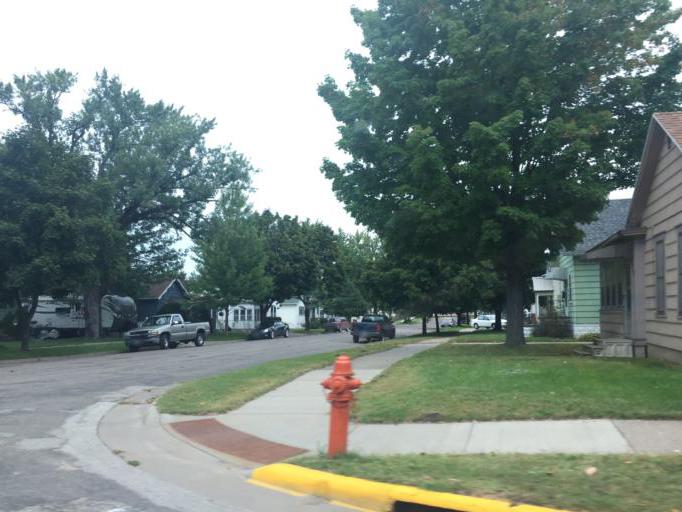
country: US
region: Minnesota
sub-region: Winona County
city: Winona
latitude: 44.0450
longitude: -91.6494
